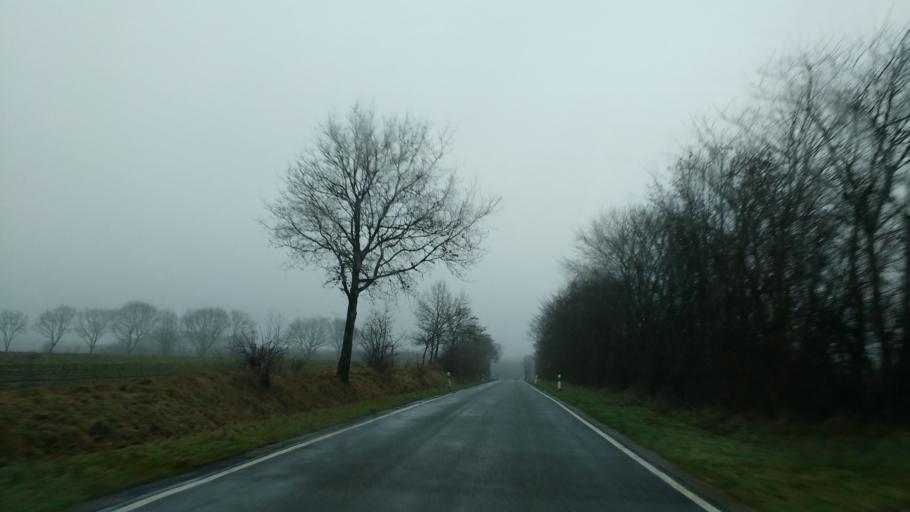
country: DE
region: Schleswig-Holstein
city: Nindorf
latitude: 54.1376
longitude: 9.6941
